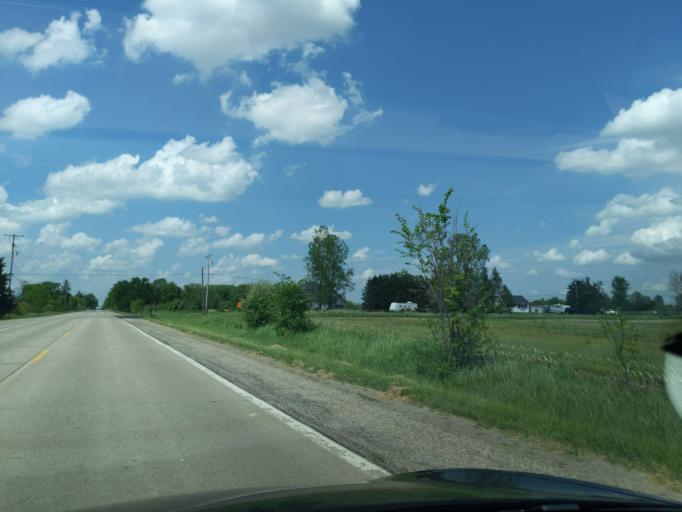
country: US
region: Michigan
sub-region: Ingham County
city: Mason
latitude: 42.6503
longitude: -84.4329
